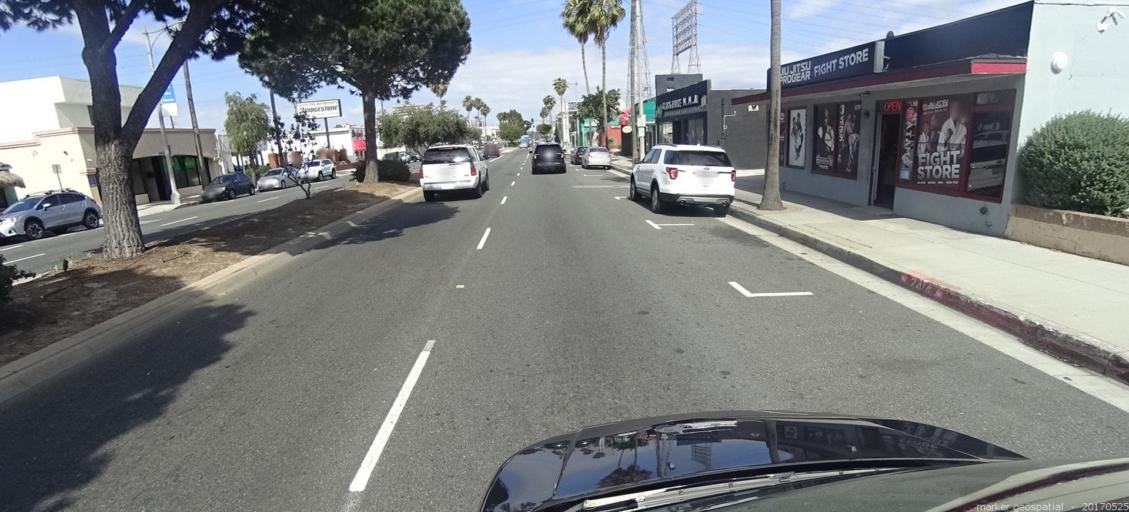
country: US
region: California
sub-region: Los Angeles County
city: Lawndale
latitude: 33.8729
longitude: -118.3674
